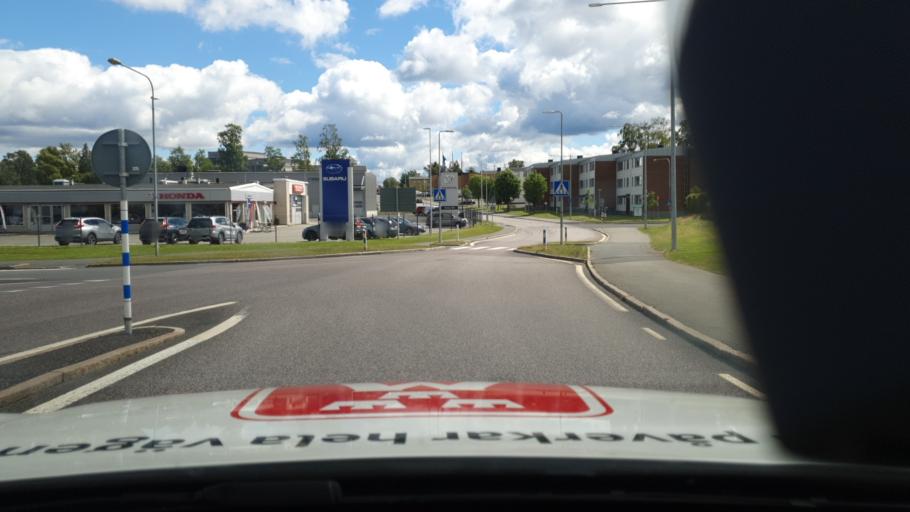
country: SE
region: Joenkoeping
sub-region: Habo Kommun
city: Habo
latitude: 57.9080
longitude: 14.0695
